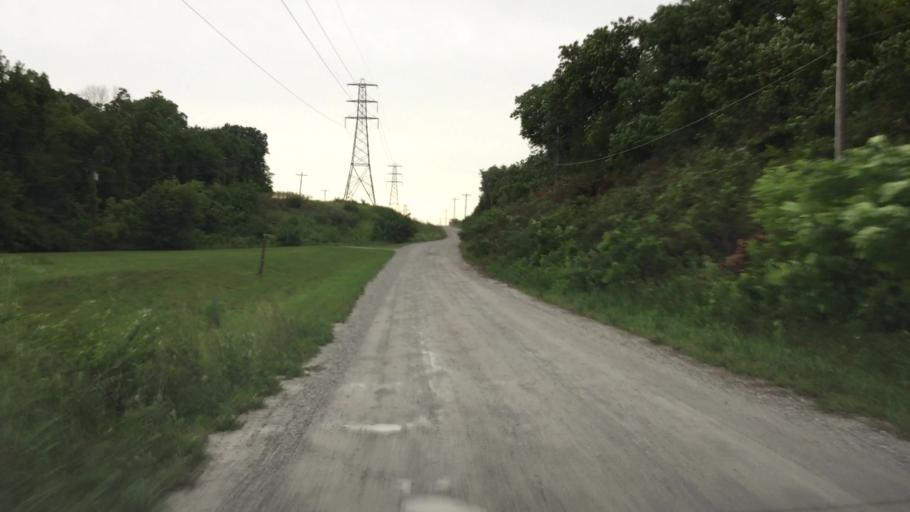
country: US
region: Illinois
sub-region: Hancock County
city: Hamilton
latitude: 40.3668
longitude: -91.3613
